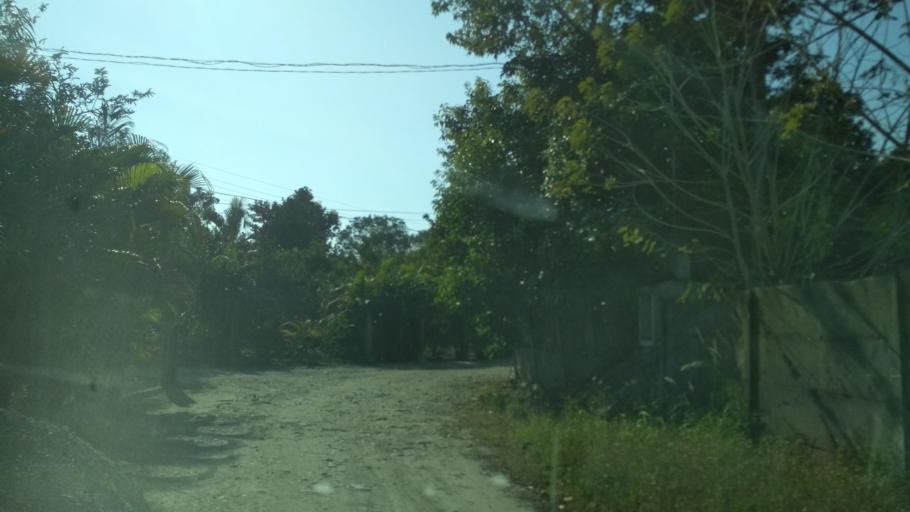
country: MX
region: Veracruz
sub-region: Martinez de la Torre
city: El Progreso
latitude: 20.0808
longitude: -97.0187
